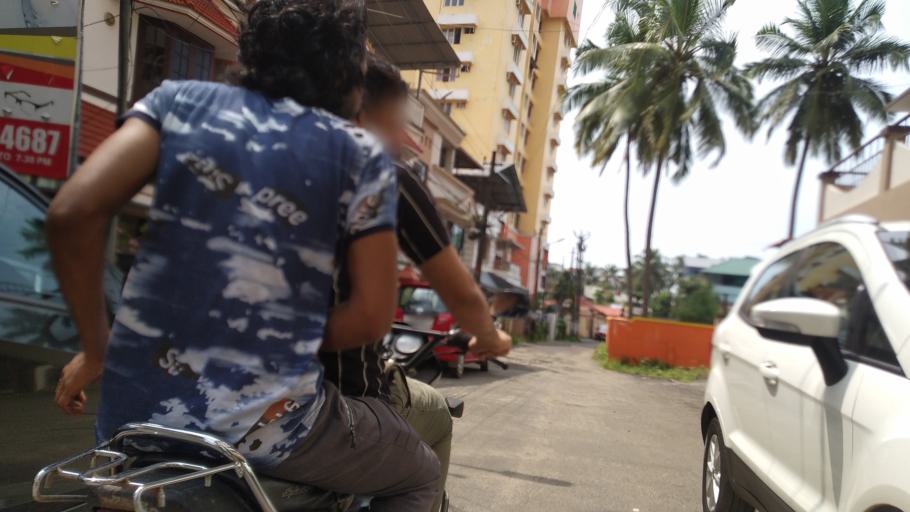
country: IN
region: Kerala
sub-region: Ernakulam
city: Cochin
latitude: 9.9694
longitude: 76.3042
